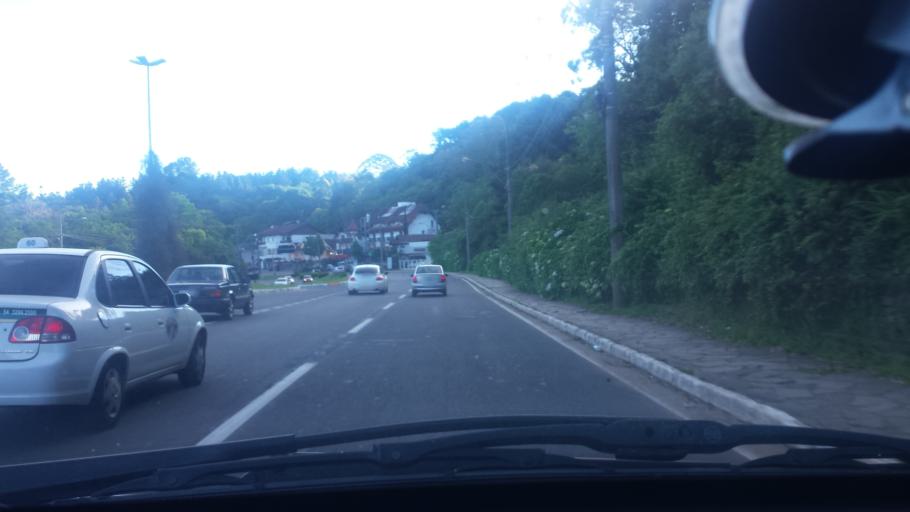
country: BR
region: Rio Grande do Sul
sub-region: Canela
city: Canela
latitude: -29.3720
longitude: -50.8638
